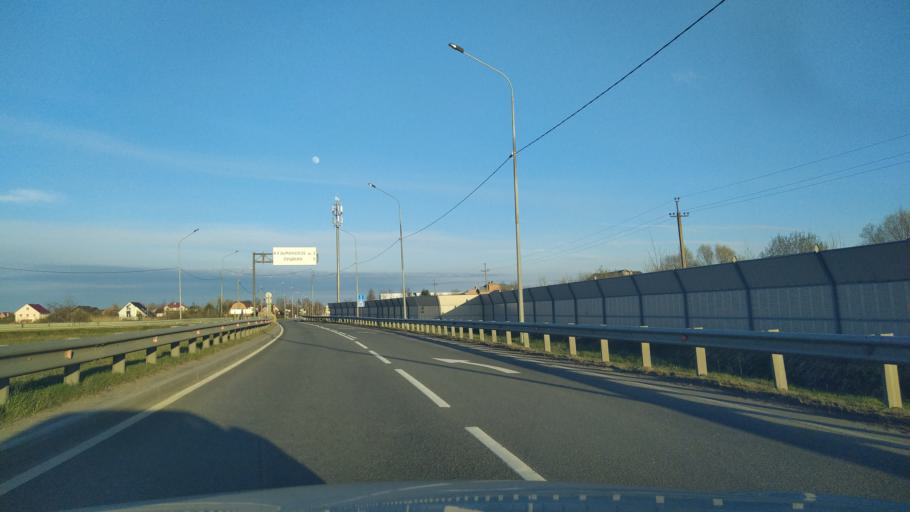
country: RU
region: St.-Petersburg
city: Aleksandrovskaya
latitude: 59.7402
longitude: 30.3206
